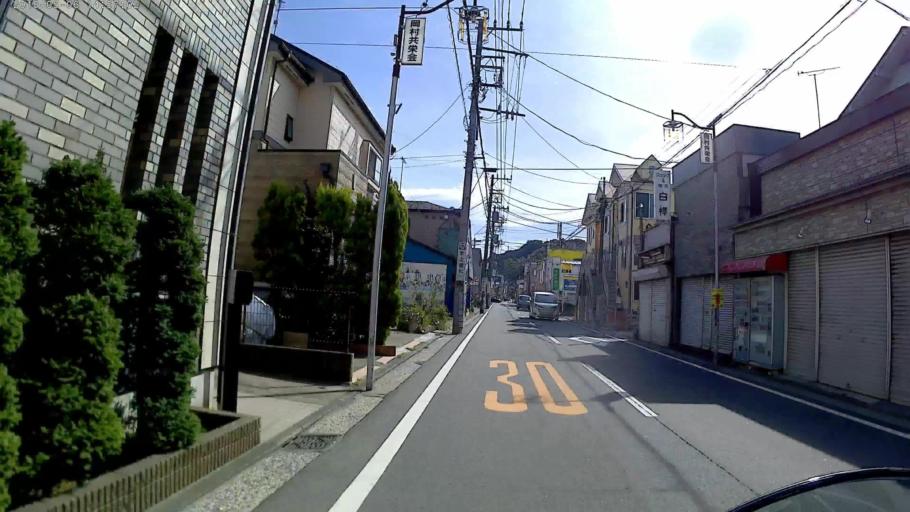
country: JP
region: Kanagawa
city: Yokohama
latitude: 35.4188
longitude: 139.6194
